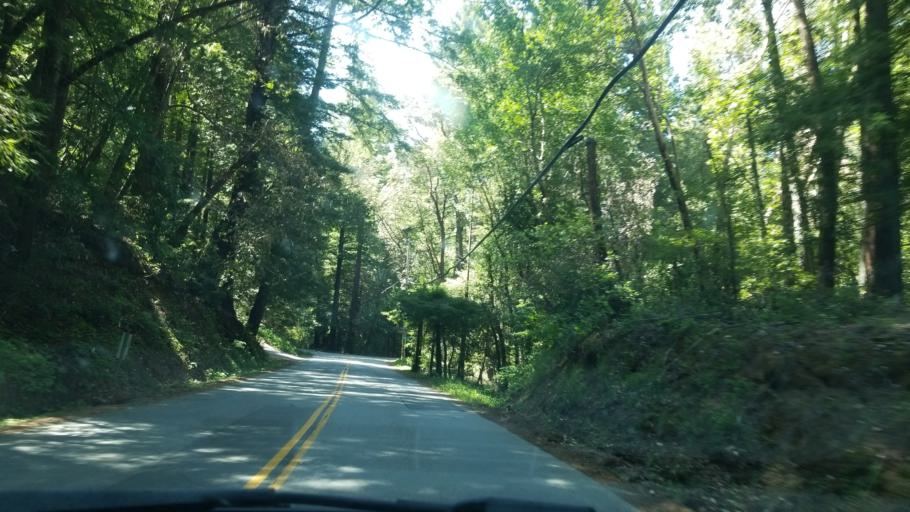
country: US
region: California
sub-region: Santa Clara County
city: Lexington Hills
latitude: 37.1128
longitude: -121.9163
